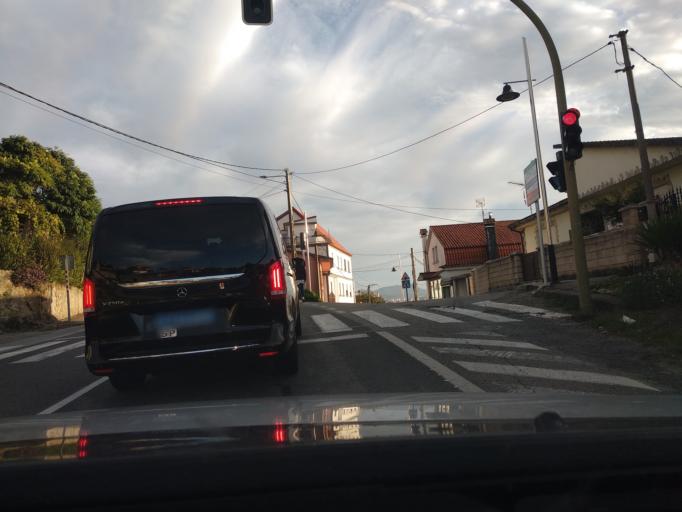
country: ES
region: Galicia
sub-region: Provincia de Pontevedra
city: Moana
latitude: 42.2812
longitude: -8.7111
